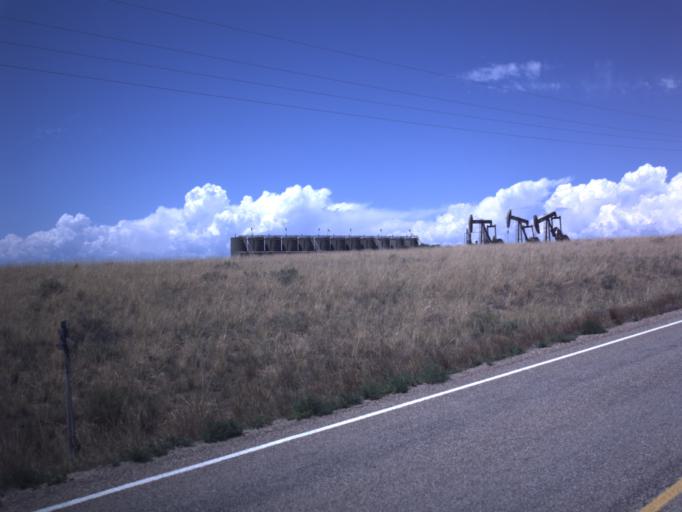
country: US
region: Utah
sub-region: Uintah County
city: Naples
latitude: 40.1537
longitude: -109.6642
